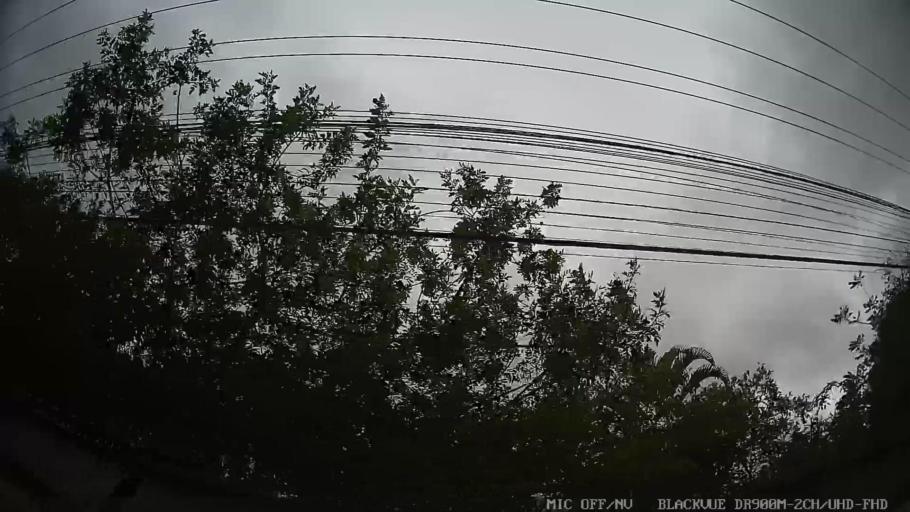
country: BR
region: Sao Paulo
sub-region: Osasco
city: Osasco
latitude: -23.4718
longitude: -46.7545
